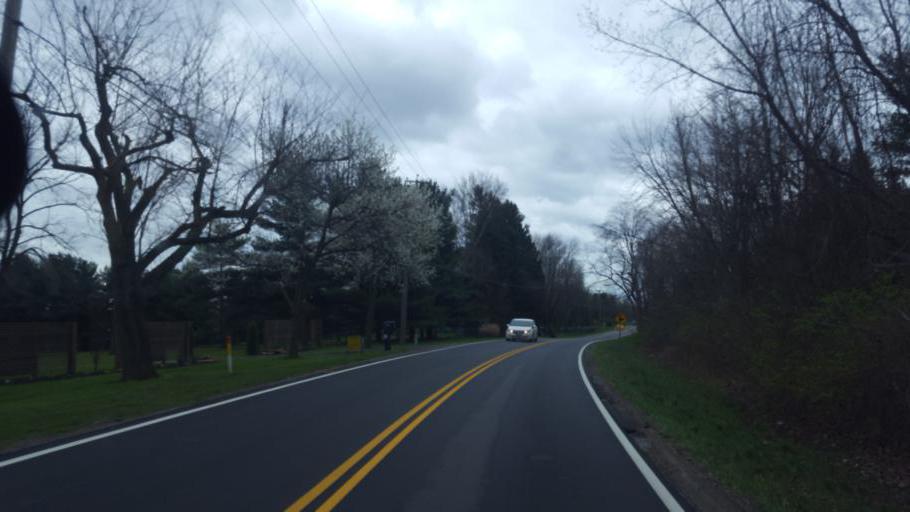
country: US
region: Ohio
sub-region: Franklin County
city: Westerville
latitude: 40.1637
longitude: -82.8778
